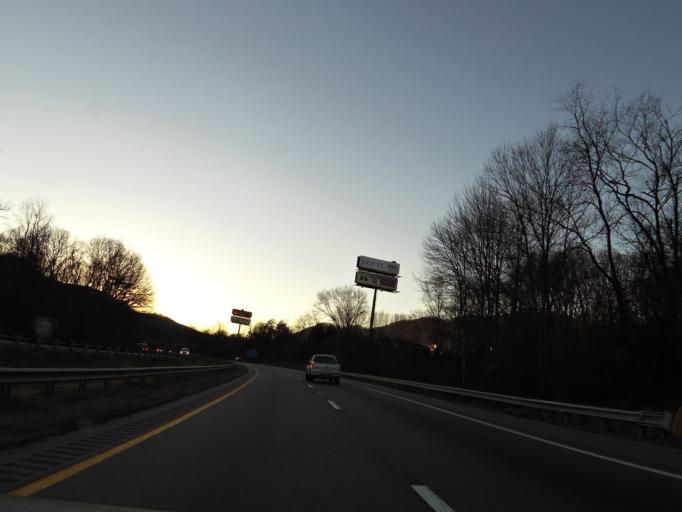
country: US
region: North Carolina
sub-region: Haywood County
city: Canton
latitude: 35.5497
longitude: -82.7396
